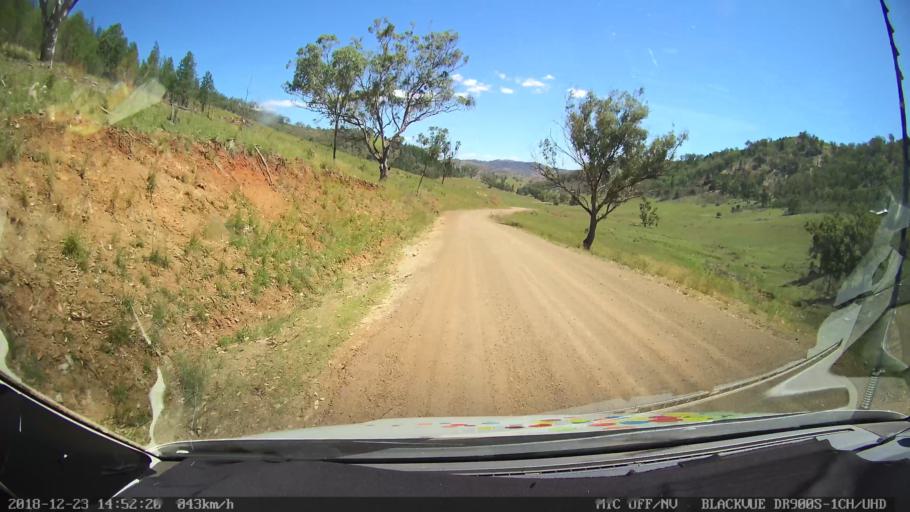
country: AU
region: New South Wales
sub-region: Tamworth Municipality
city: Manilla
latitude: -30.6834
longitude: 150.8545
